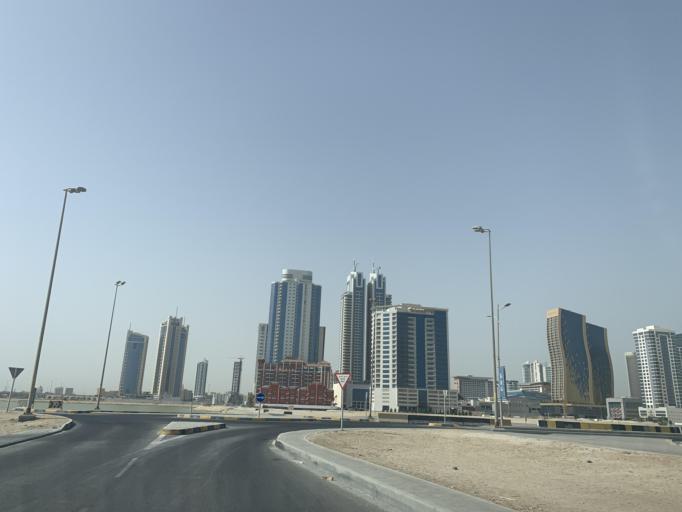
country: BH
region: Manama
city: Jidd Hafs
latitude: 26.2414
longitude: 50.5572
